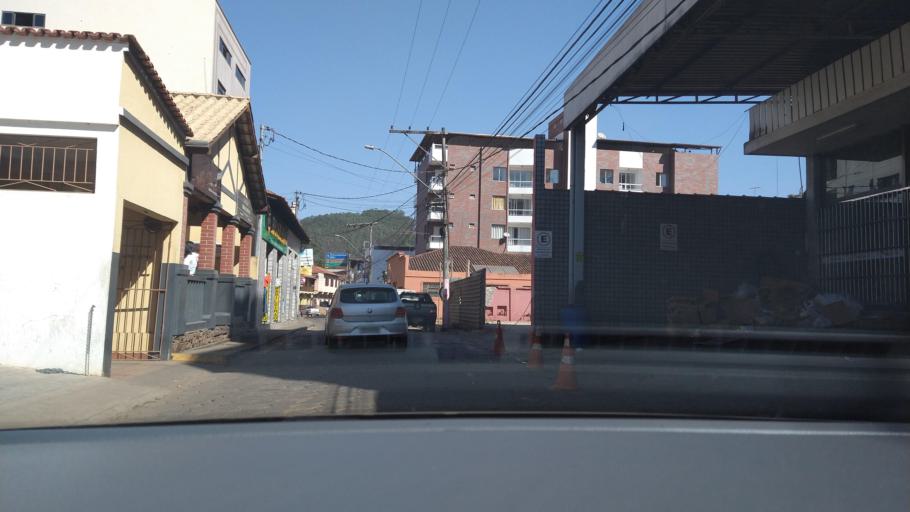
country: BR
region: Minas Gerais
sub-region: Rio Piracicaba
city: Rio Piracicaba
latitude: -19.9305
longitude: -43.1743
